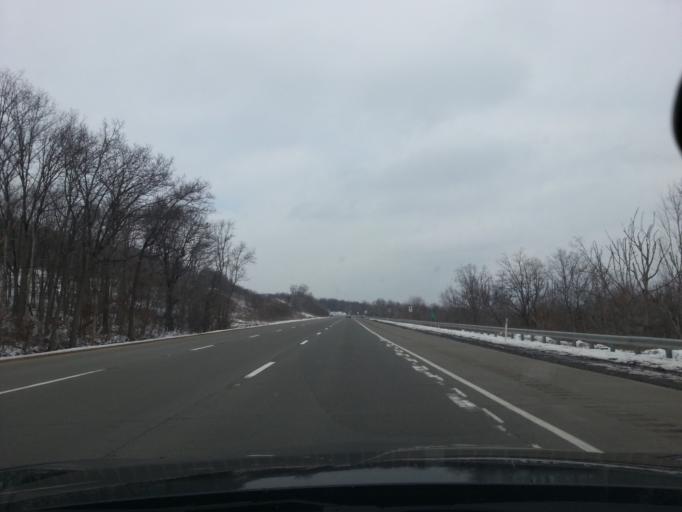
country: US
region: Pennsylvania
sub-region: Luzerne County
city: Harleigh
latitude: 41.0578
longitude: -75.9967
